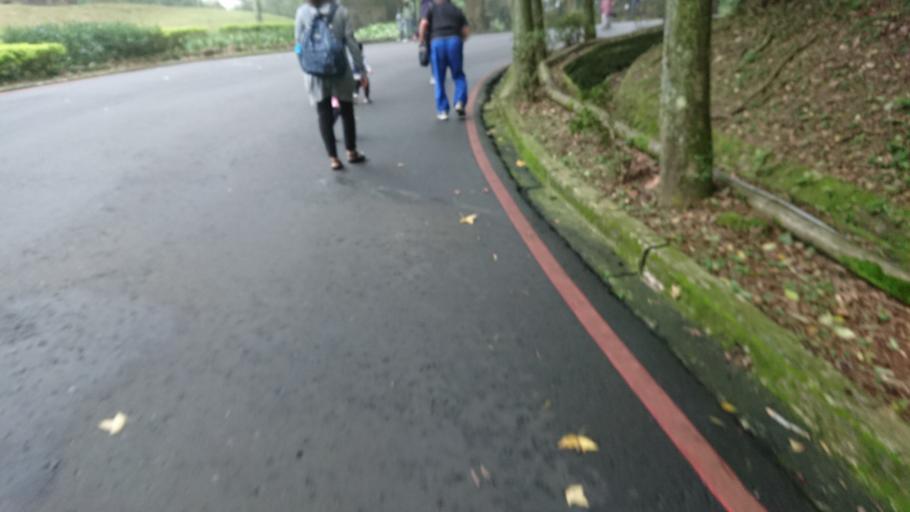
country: TW
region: Taiwan
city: Daxi
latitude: 24.8161
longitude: 121.2414
